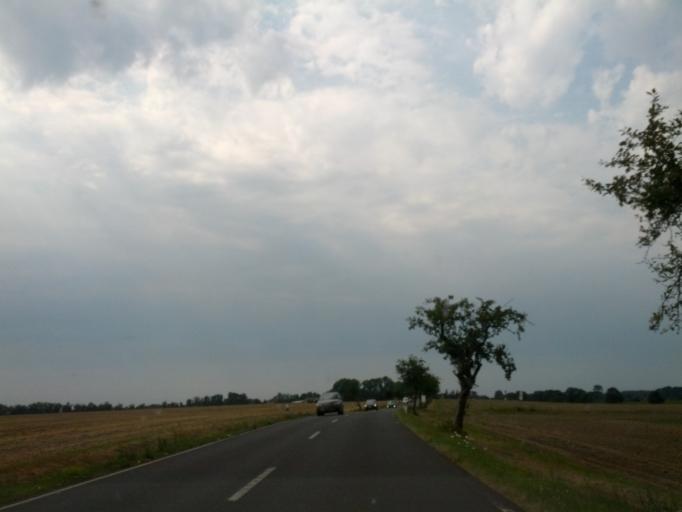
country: DE
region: Brandenburg
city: Kremmen
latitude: 52.7517
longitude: 12.9020
